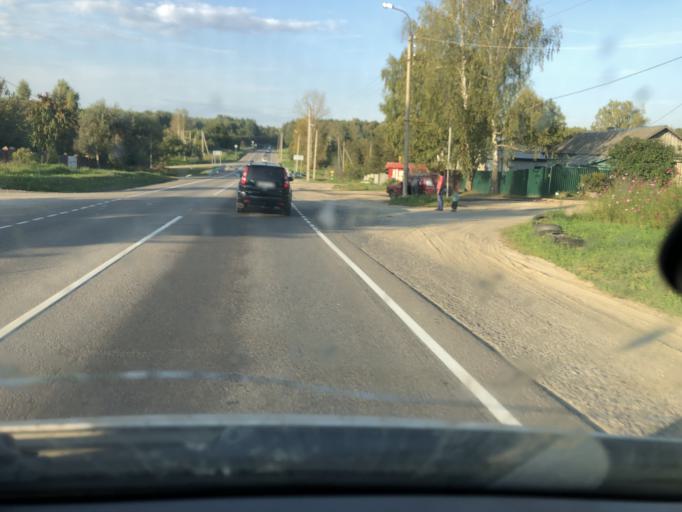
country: RU
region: Kaluga
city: Peremyshl'
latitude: 54.3825
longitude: 36.2009
